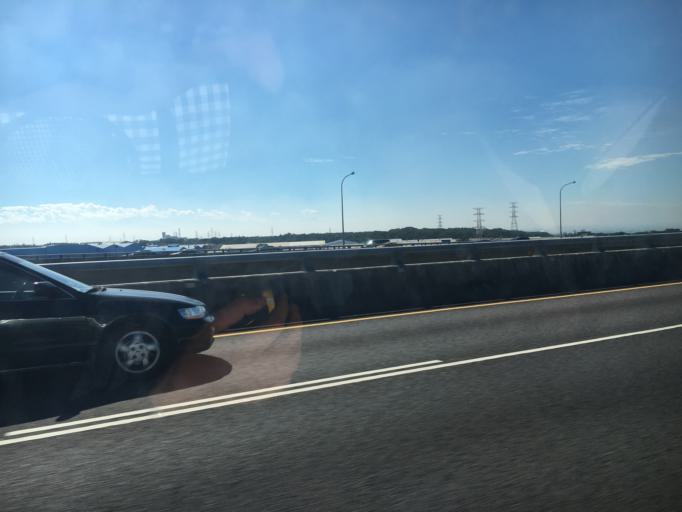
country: TW
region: Taiwan
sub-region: Taoyuan
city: Taoyuan
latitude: 25.0659
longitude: 121.3472
